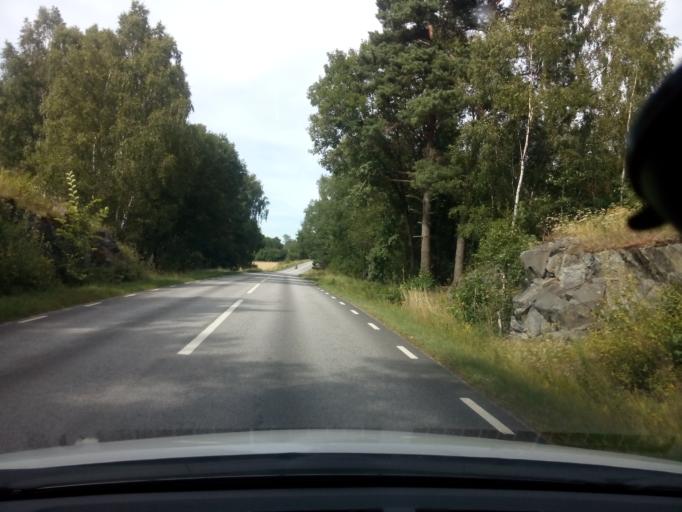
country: SE
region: Soedermanland
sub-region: Oxelosunds Kommun
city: Bara
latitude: 58.7589
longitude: 17.1120
